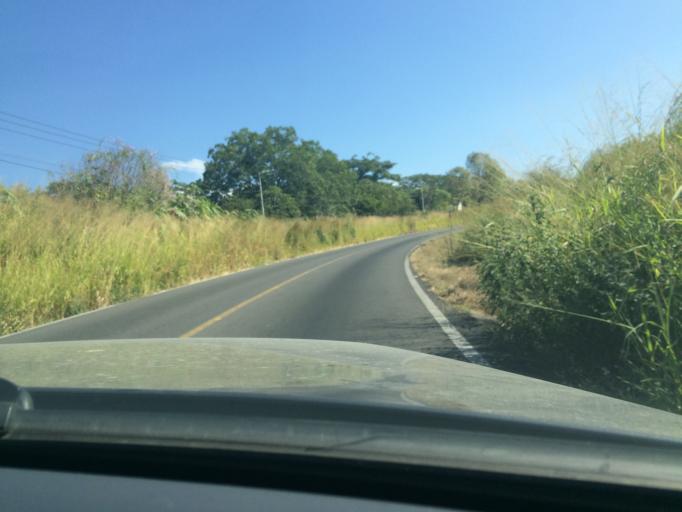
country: MX
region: Colima
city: Suchitlan
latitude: 19.3548
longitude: -103.7316
